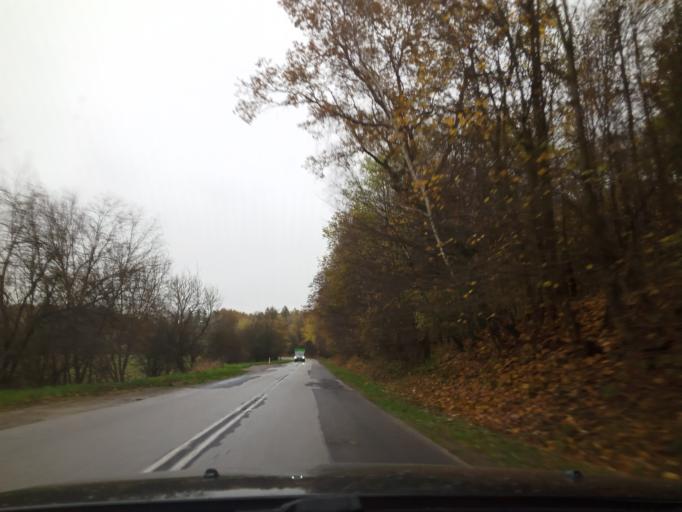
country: PL
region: Swietokrzyskie
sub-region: Powiat pinczowski
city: Dzialoszyce
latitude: 50.4159
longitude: 20.3304
